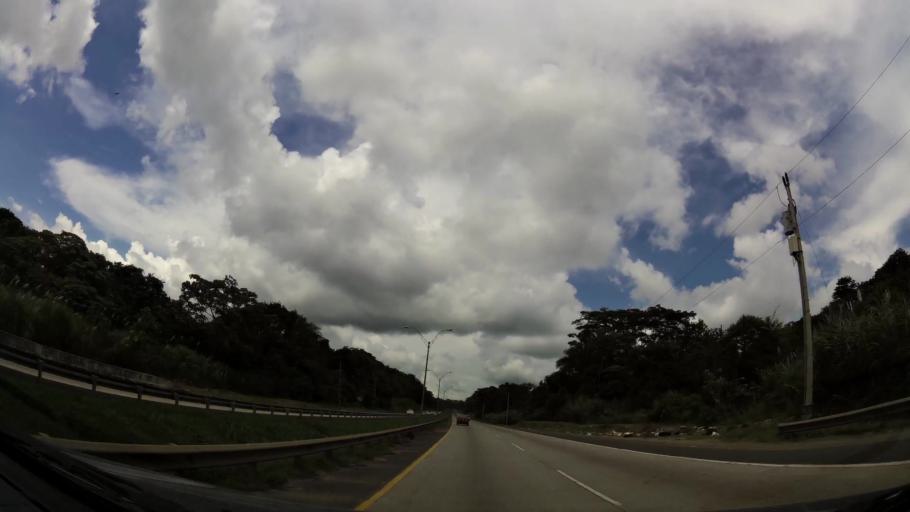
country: PA
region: Panama
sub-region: Distrito Arraijan
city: Arraijan
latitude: 8.9745
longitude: -79.6440
